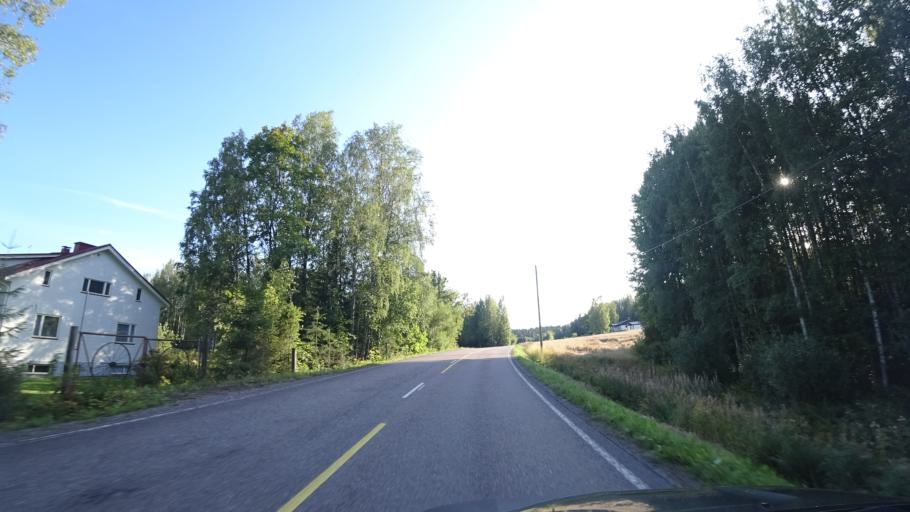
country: FI
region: Paijanne Tavastia
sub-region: Lahti
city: Asikkala
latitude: 61.1795
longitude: 25.3780
